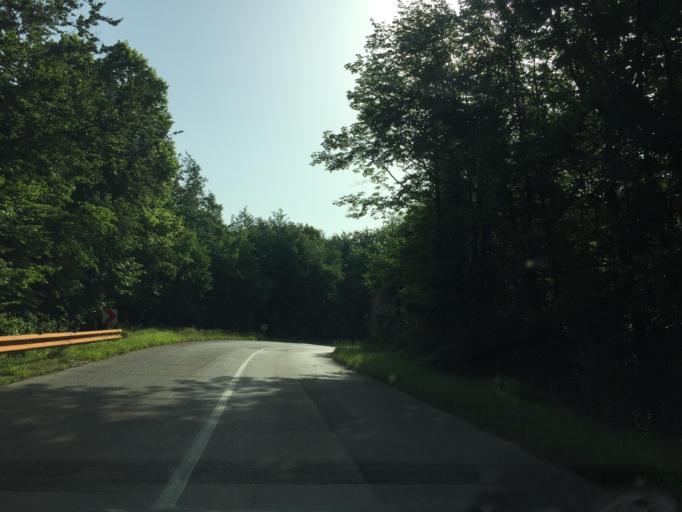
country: HR
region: Primorsko-Goranska
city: Kastav
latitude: 45.4222
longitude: 14.3277
